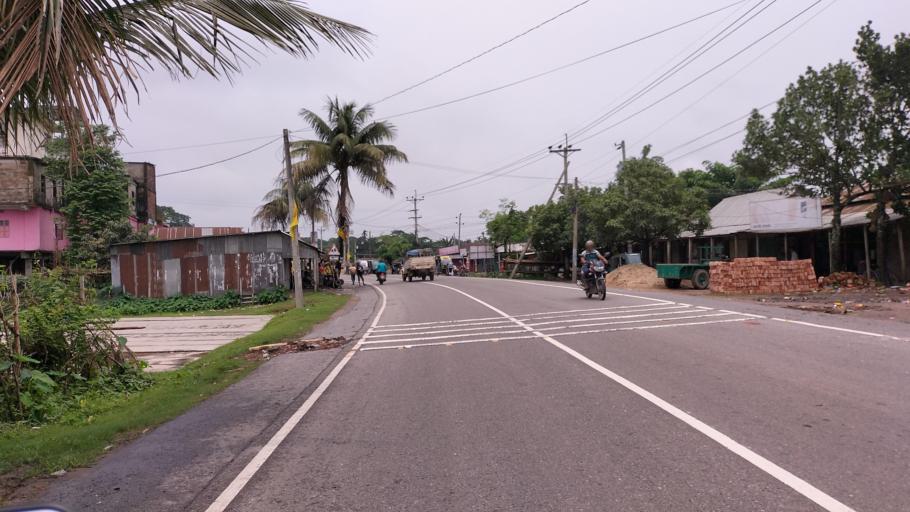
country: BD
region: Dhaka
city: Netrakona
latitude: 24.8493
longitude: 90.6435
